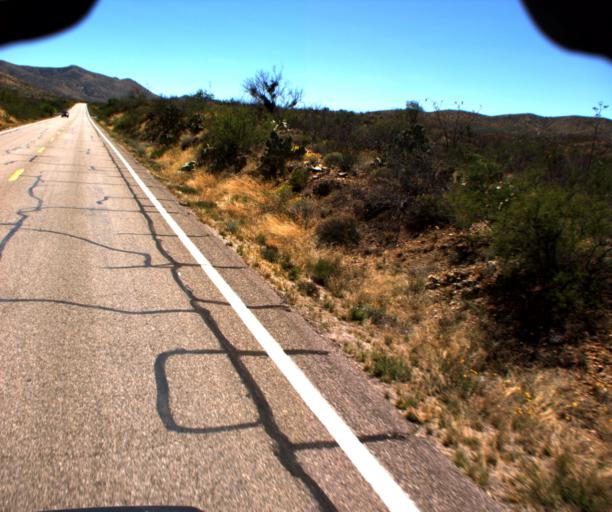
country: US
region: Arizona
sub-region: Pima County
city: Corona de Tucson
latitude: 31.9375
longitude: -110.6615
